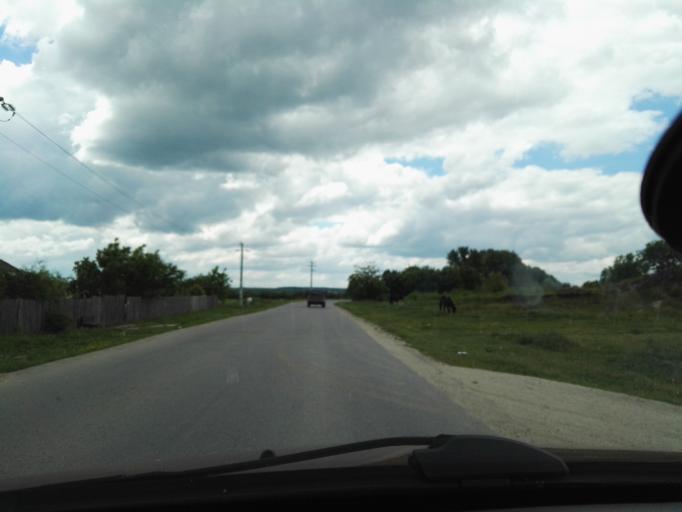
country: RO
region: Giurgiu
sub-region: Comuna Comana
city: Gradistea
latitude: 44.2079
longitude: 26.1489
